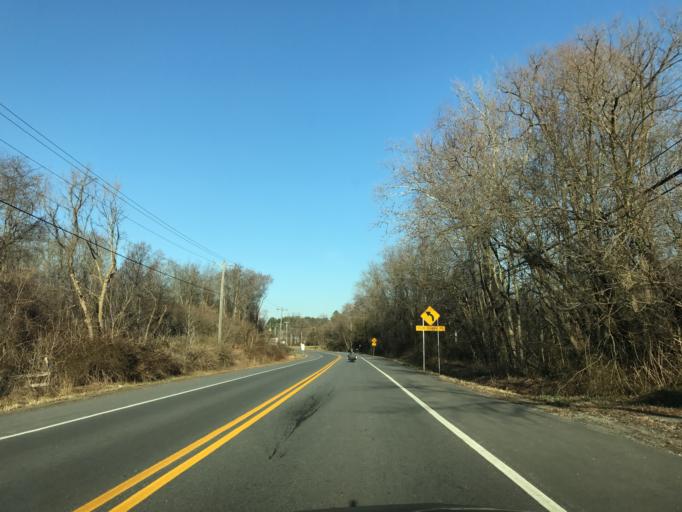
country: US
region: Delaware
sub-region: New Castle County
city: Townsend
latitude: 39.2530
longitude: -75.8449
